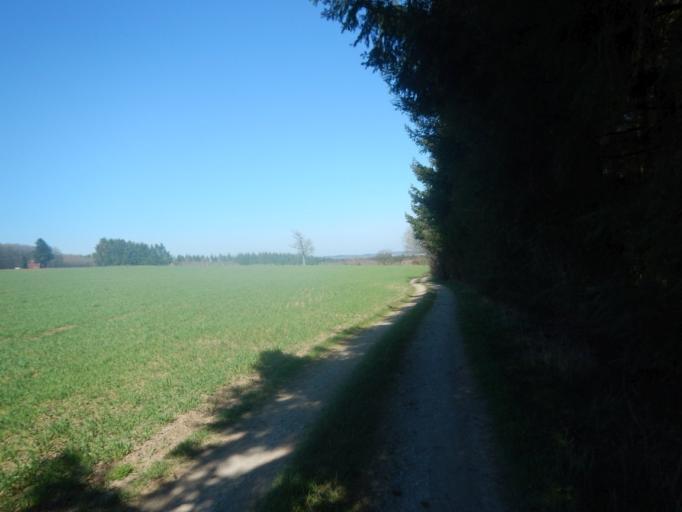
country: LU
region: Diekirch
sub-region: Canton de Wiltz
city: Goesdorf
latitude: 49.9496
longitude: 5.9638
